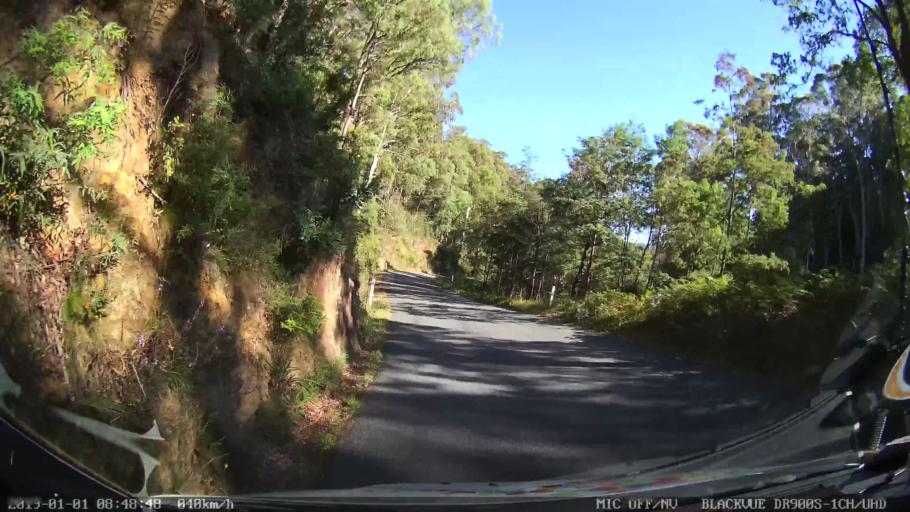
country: AU
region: New South Wales
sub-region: Snowy River
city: Jindabyne
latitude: -36.2867
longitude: 148.1988
